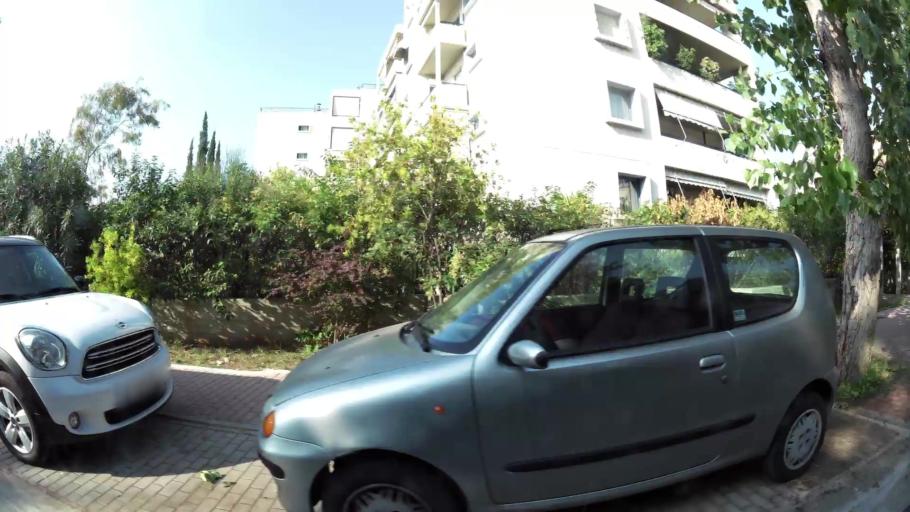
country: GR
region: Attica
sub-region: Nomarchia Athinas
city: Cholargos
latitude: 38.0047
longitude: 23.8092
